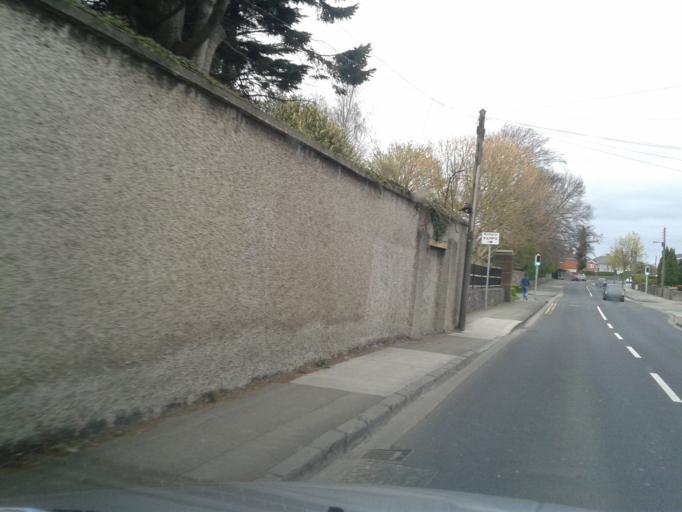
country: IE
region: Leinster
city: Marino
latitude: 53.3788
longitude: -6.2408
